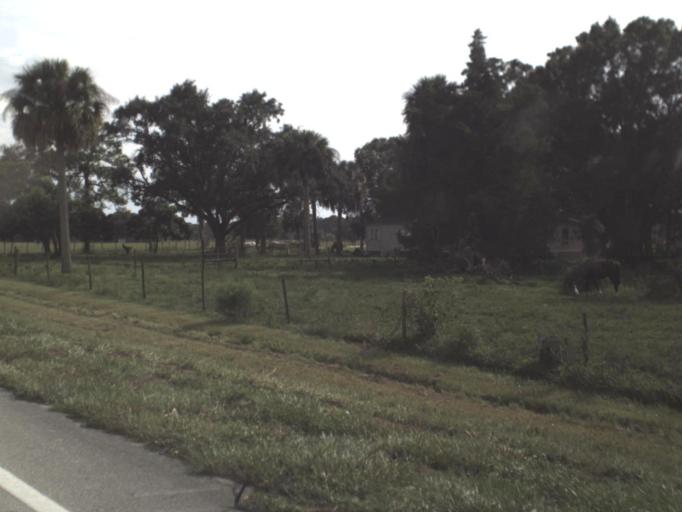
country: US
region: Florida
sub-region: Okeechobee County
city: Taylor Creek
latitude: 27.2328
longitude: -80.7757
